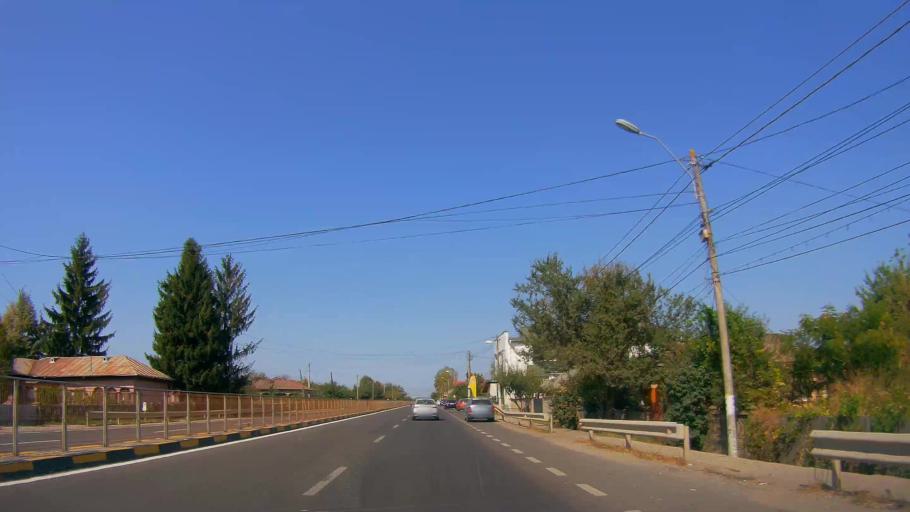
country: RO
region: Giurgiu
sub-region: Comuna Fratesti
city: Remus
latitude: 43.9404
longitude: 25.9783
